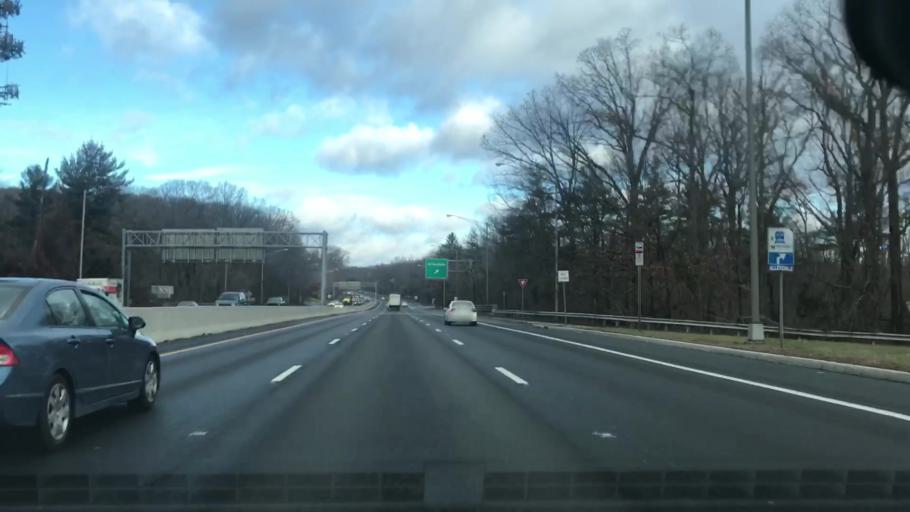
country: US
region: New Jersey
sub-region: Bergen County
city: Saddle River
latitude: 41.0311
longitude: -74.1109
